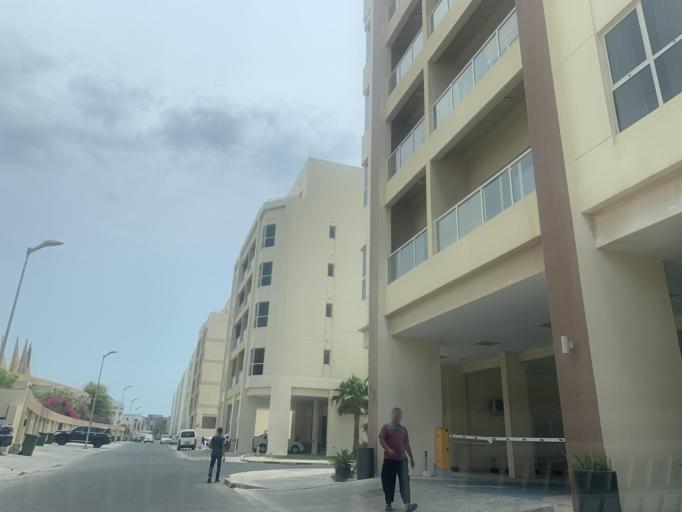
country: BH
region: Muharraq
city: Al Hadd
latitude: 26.2873
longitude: 50.6695
